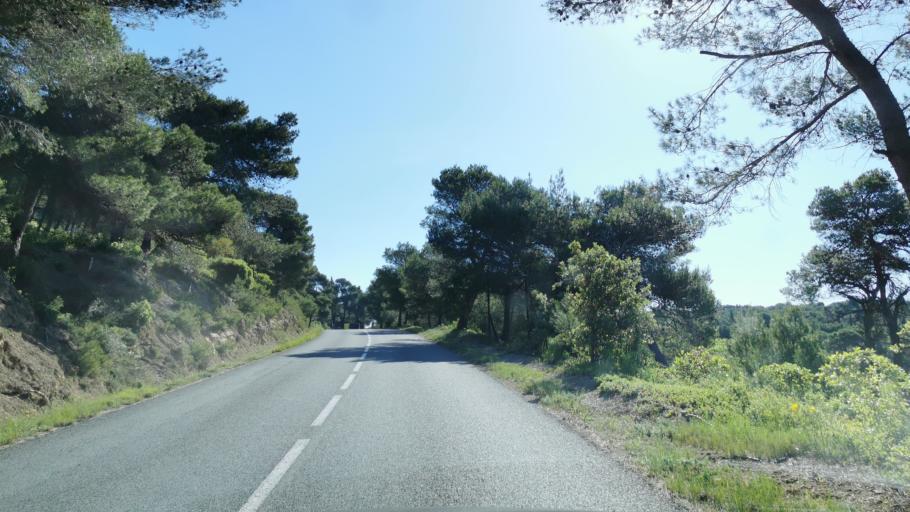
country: FR
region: Languedoc-Roussillon
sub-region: Departement de l'Aude
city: Armissan
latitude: 43.1691
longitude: 3.1186
